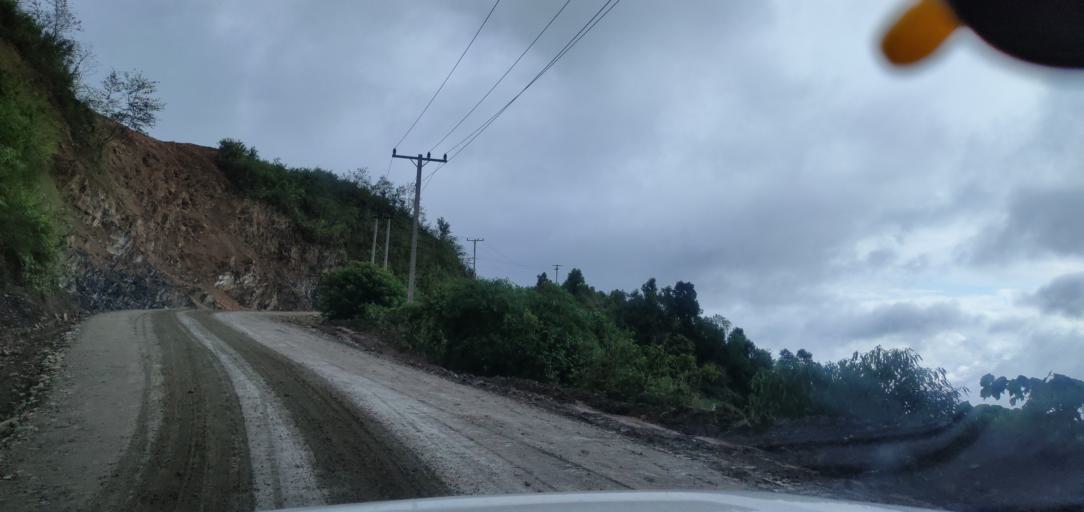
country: LA
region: Phongsali
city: Phongsali
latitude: 21.4240
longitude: 102.1712
